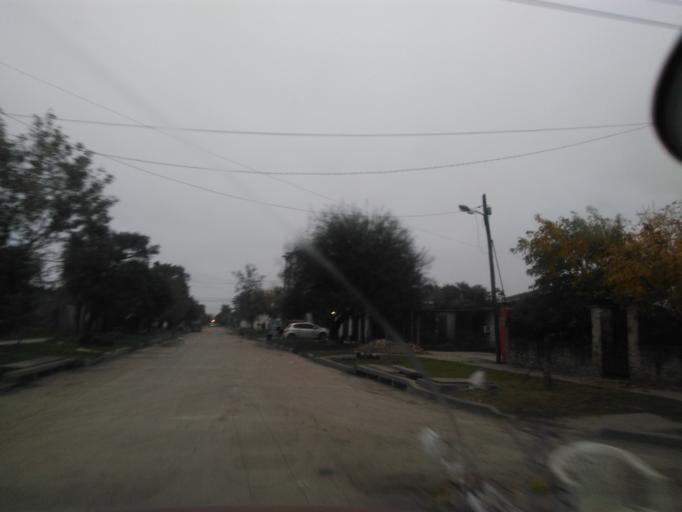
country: AR
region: Chaco
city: Resistencia
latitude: -27.4776
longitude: -58.9982
